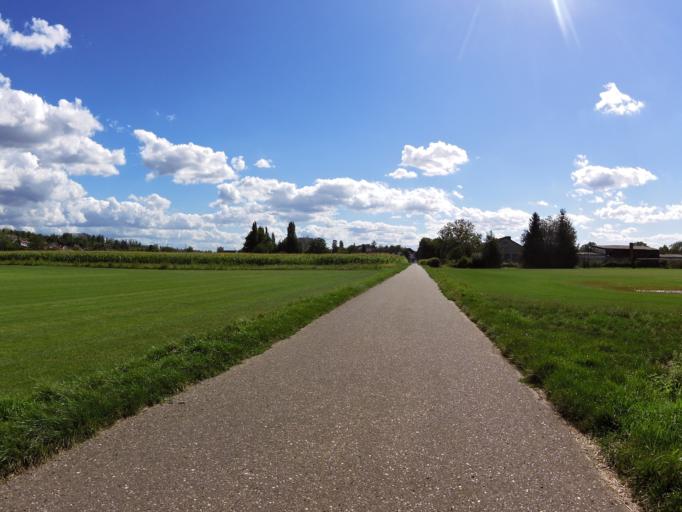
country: DE
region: Baden-Wuerttemberg
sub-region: Freiburg Region
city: Lahr
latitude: 48.3520
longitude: 7.8414
